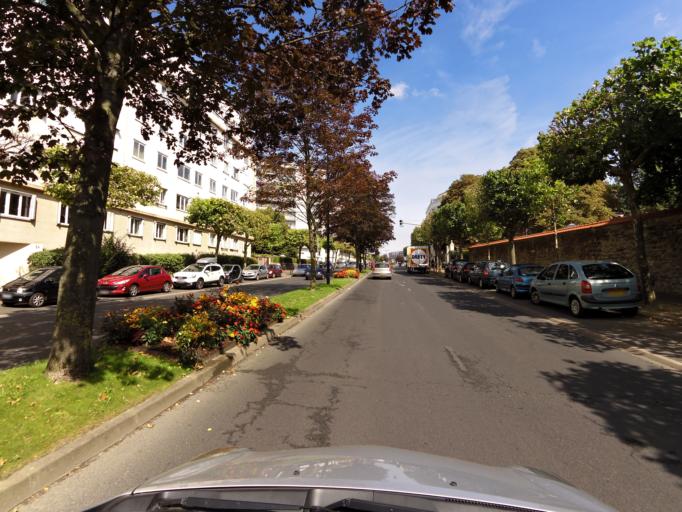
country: FR
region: Ile-de-France
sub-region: Departement du Val-de-Marne
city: Joinville-le-Pont
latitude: 48.8133
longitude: 2.4685
